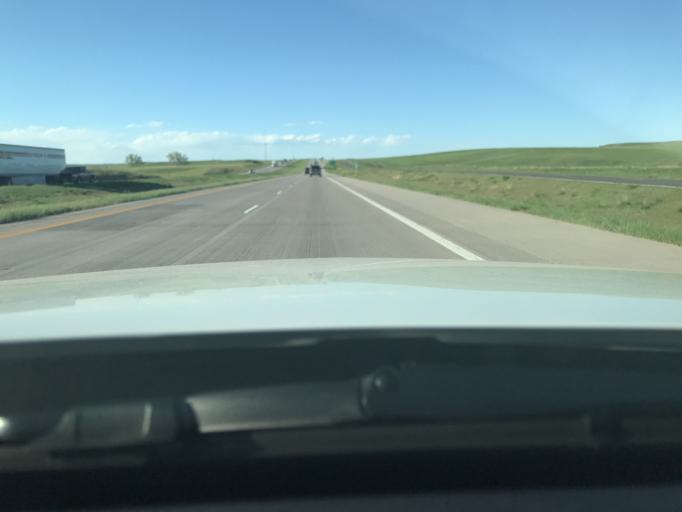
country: US
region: Colorado
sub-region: Larimer County
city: Wellington
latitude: 40.8324
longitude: -104.9690
